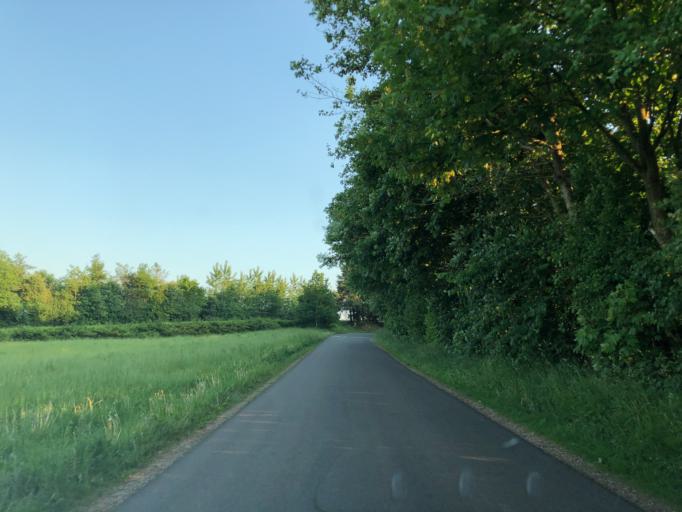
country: DK
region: Central Jutland
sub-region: Struer Kommune
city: Struer
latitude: 56.4307
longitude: 8.5054
